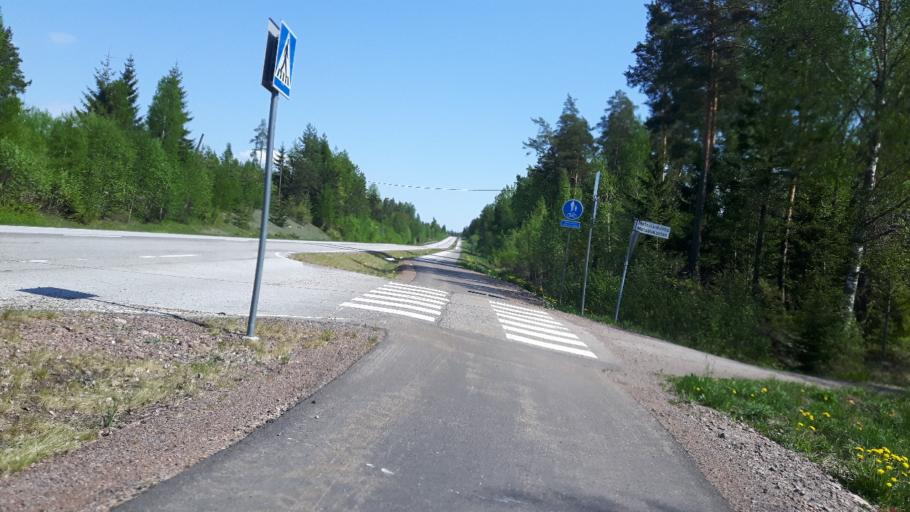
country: FI
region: Uusimaa
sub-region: Loviisa
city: Ruotsinpyhtaeae
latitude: 60.4834
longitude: 26.3939
